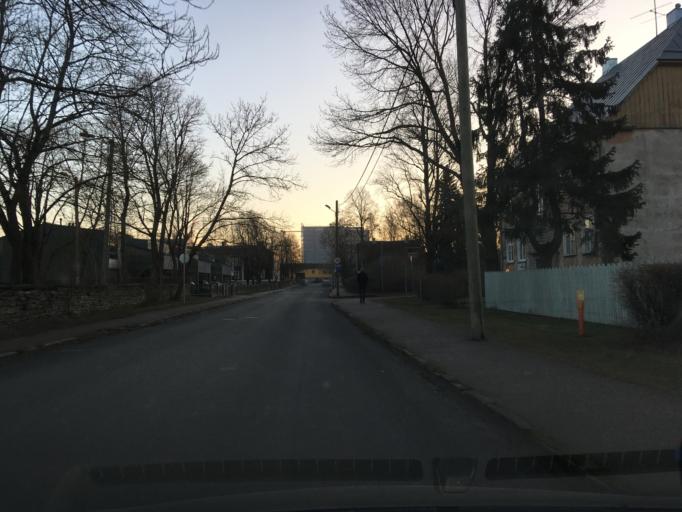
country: EE
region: Harju
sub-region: Tallinna linn
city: Tallinn
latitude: 59.4238
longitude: 24.7548
